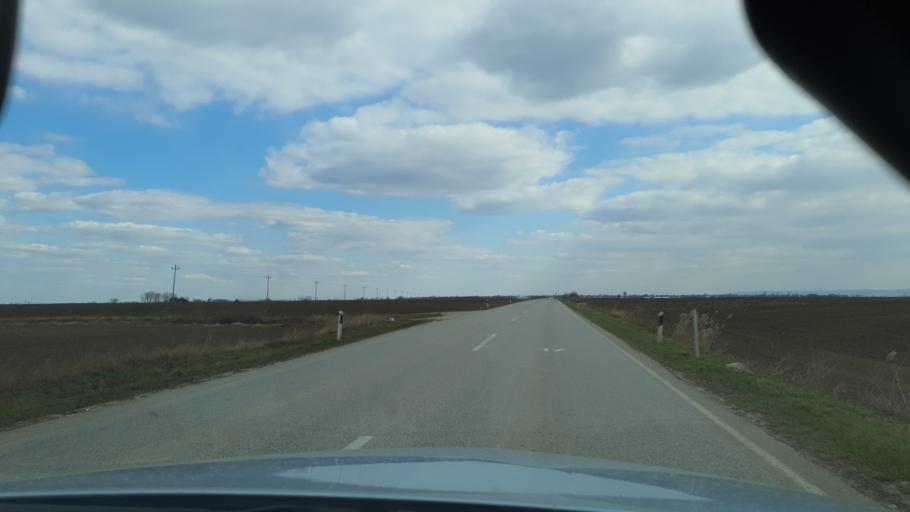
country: RS
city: Obrovac
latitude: 45.4077
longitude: 19.4200
